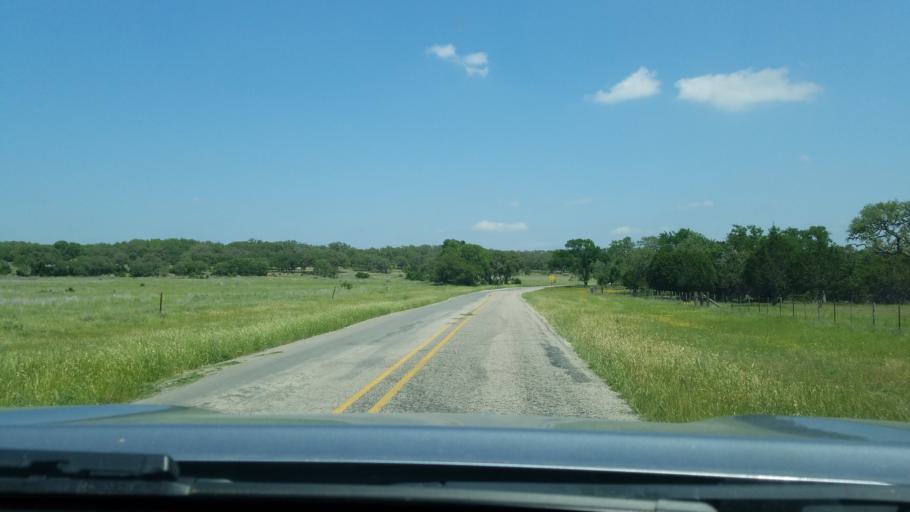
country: US
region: Texas
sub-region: Blanco County
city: Blanco
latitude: 29.9732
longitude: -98.5299
